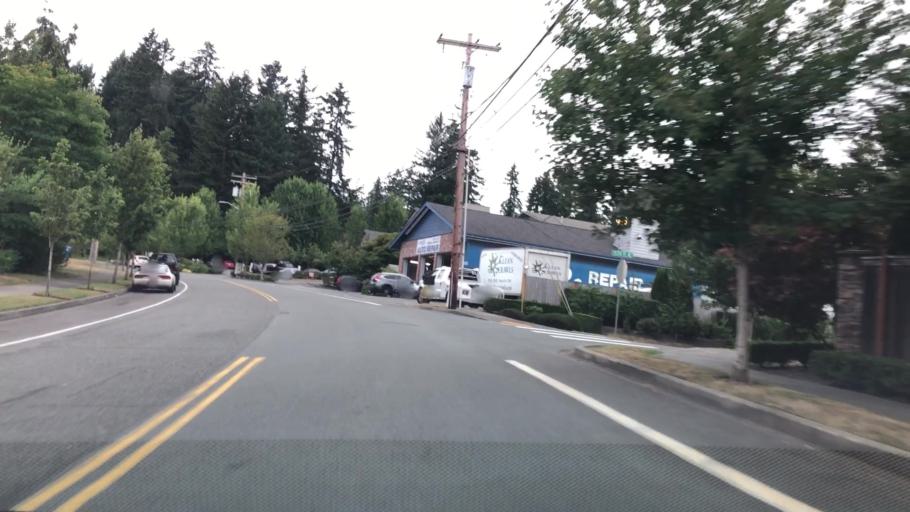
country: US
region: Washington
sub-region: King County
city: Woodinville
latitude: 47.7624
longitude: -122.1293
